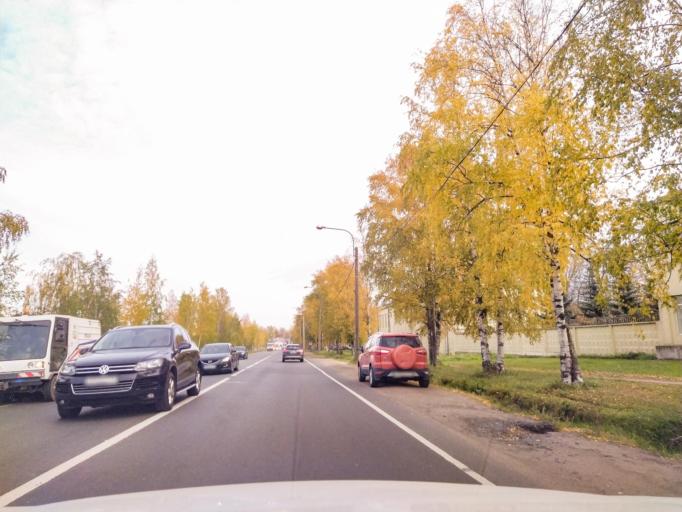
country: RU
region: St.-Petersburg
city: Tyarlevo
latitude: 59.7221
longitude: 30.4347
